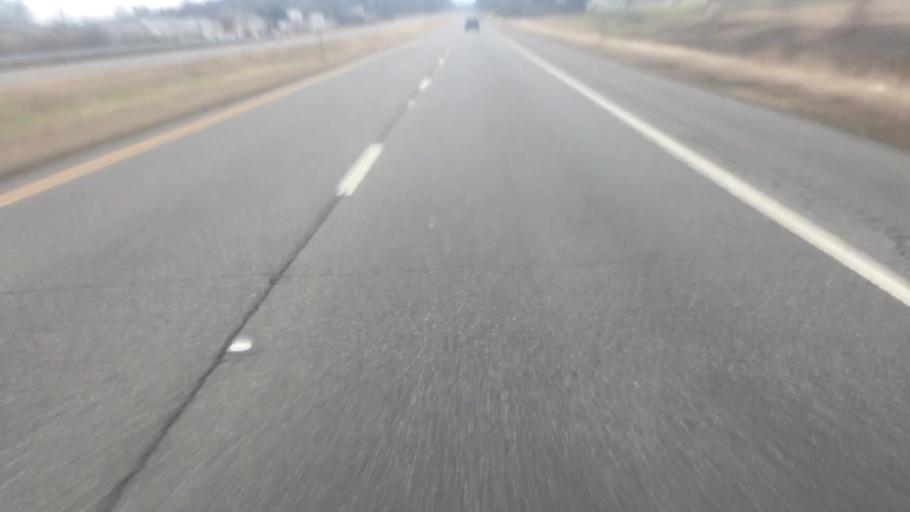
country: US
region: Alabama
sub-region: Walker County
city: Jasper
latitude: 33.8311
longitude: -87.2113
